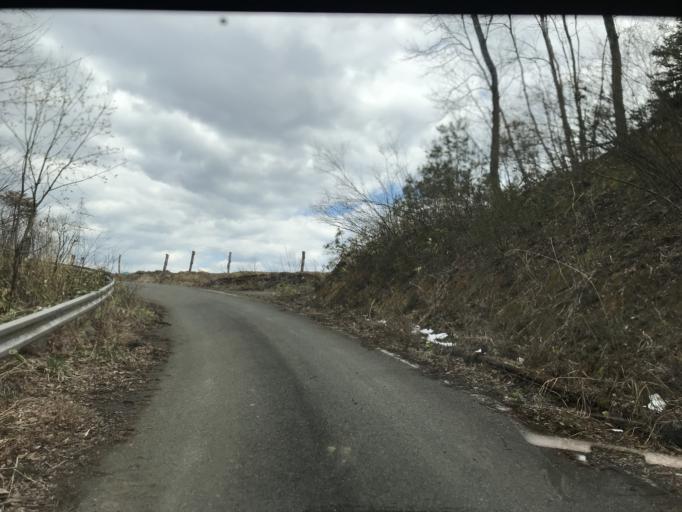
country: JP
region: Iwate
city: Ichinoseki
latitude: 38.9527
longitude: 141.0705
